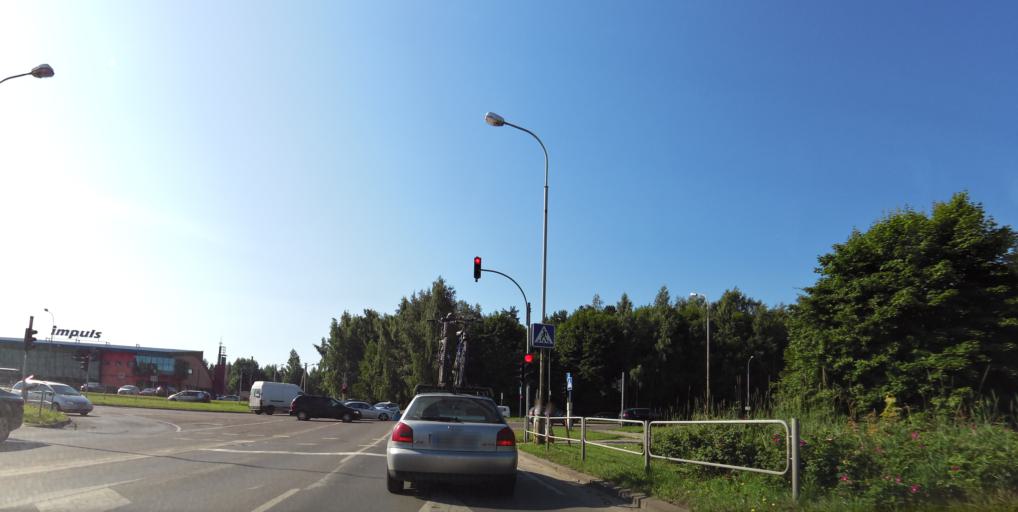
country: LT
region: Vilnius County
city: Seskine
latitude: 54.7094
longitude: 25.2402
